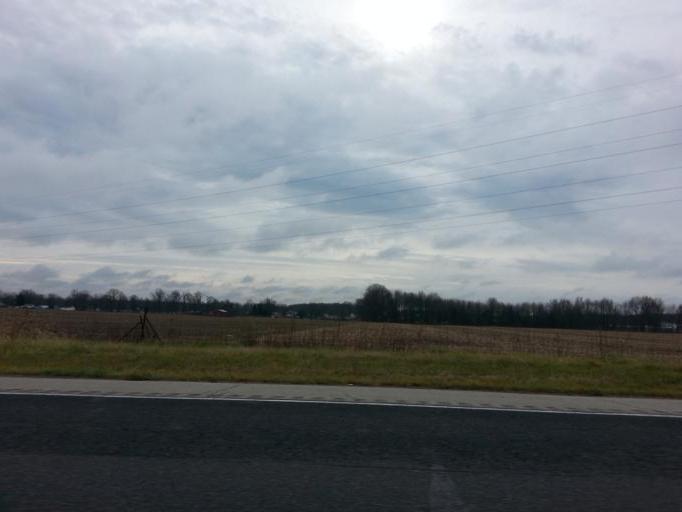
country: US
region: Indiana
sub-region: Ripley County
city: Batesville
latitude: 39.3165
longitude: -85.3307
